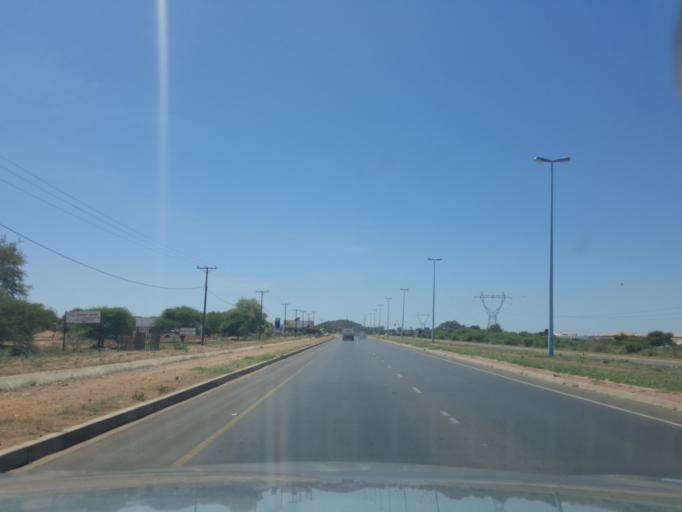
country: BW
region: Kweneng
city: Gaphatshwe
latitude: -24.5858
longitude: 25.8420
